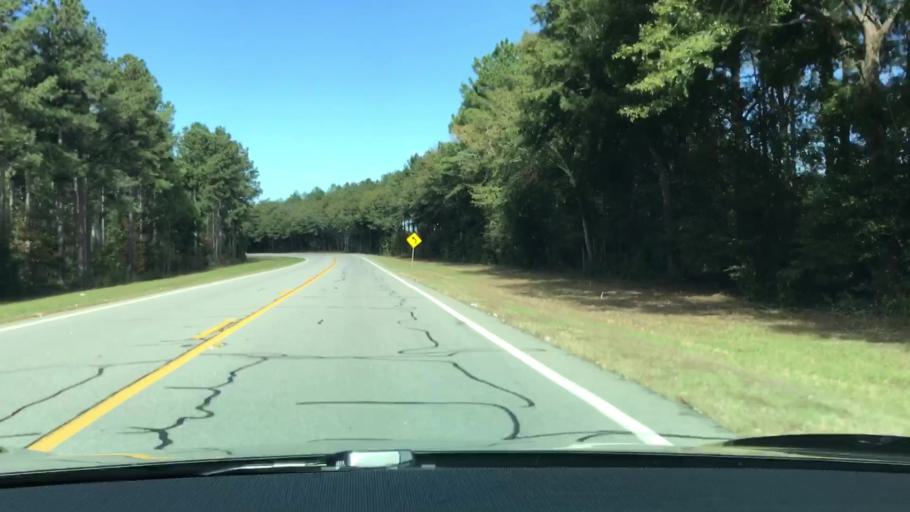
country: US
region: Georgia
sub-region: Warren County
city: Warrenton
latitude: 33.3519
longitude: -82.5862
